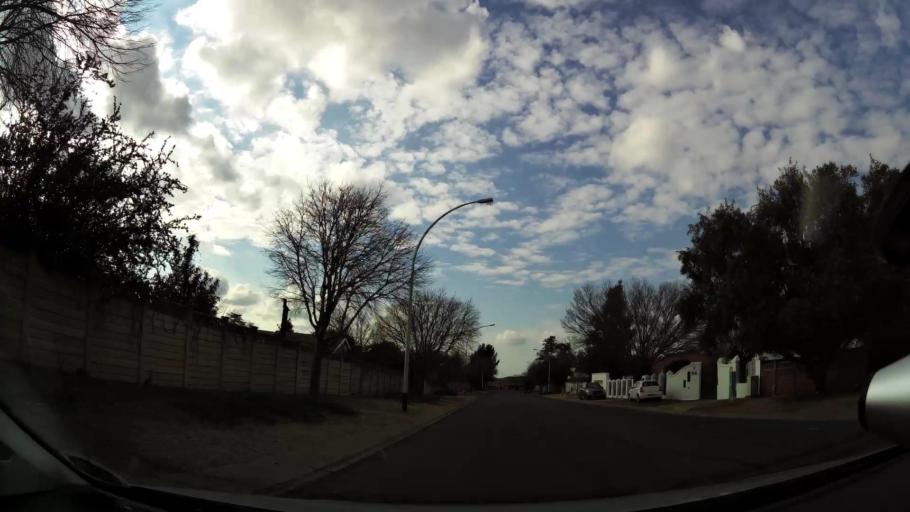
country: ZA
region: Orange Free State
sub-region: Mangaung Metropolitan Municipality
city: Bloemfontein
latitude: -29.0735
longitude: 26.2128
